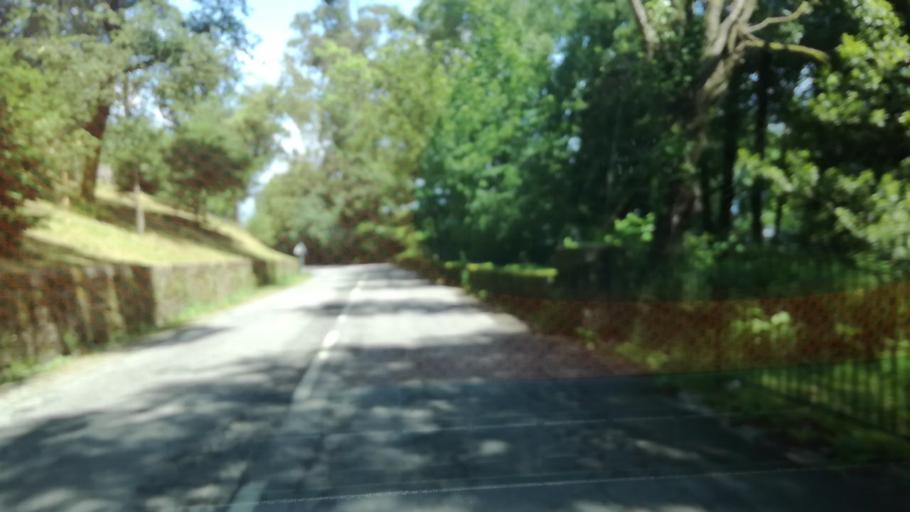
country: PT
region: Braga
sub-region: Braga
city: Adaufe
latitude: 41.5552
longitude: -8.3741
